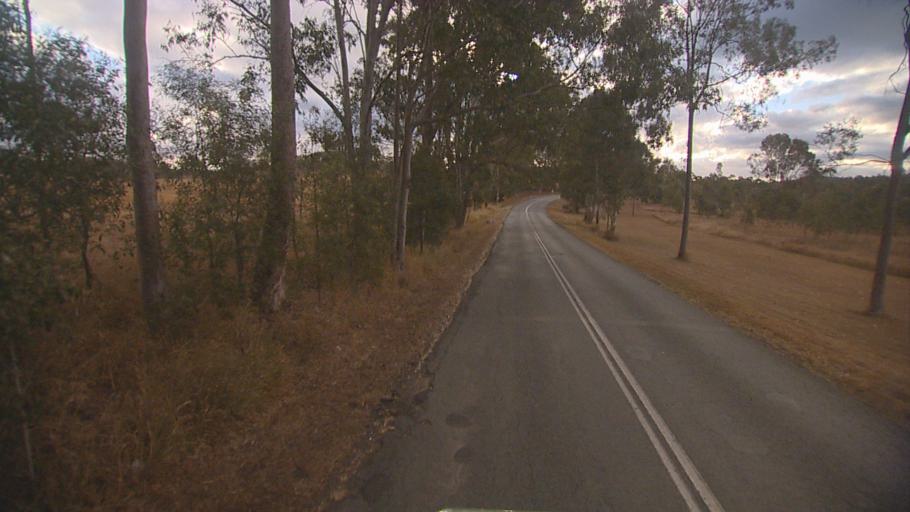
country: AU
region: Queensland
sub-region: Logan
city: Cedar Vale
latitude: -27.8826
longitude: 153.0722
